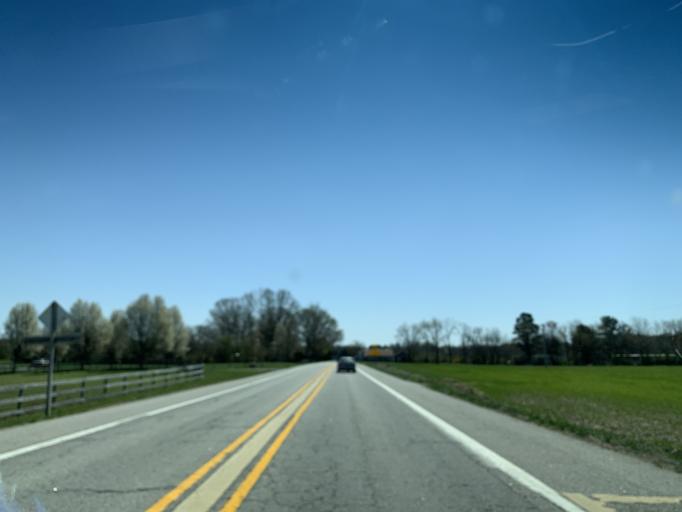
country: US
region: Maryland
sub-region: Queen Anne's County
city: Centreville
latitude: 38.9802
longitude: -76.0132
